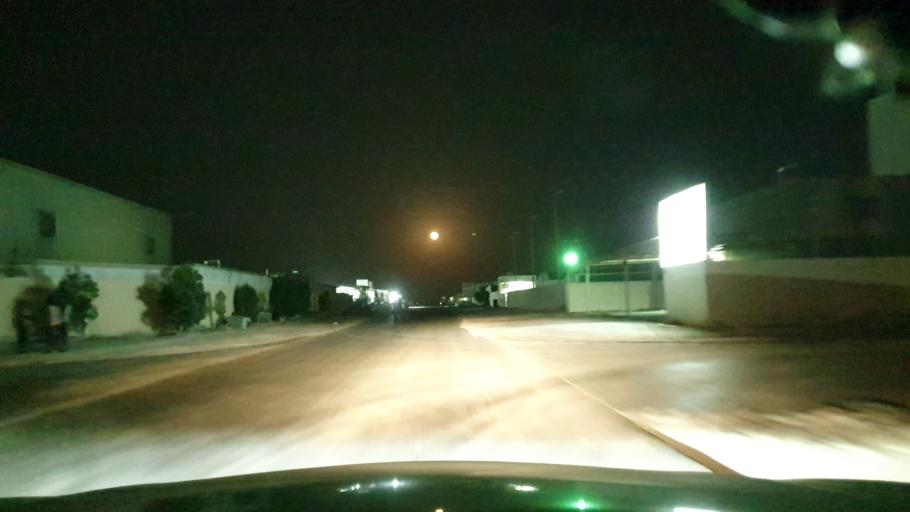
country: BH
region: Northern
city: Sitrah
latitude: 26.0973
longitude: 50.6206
